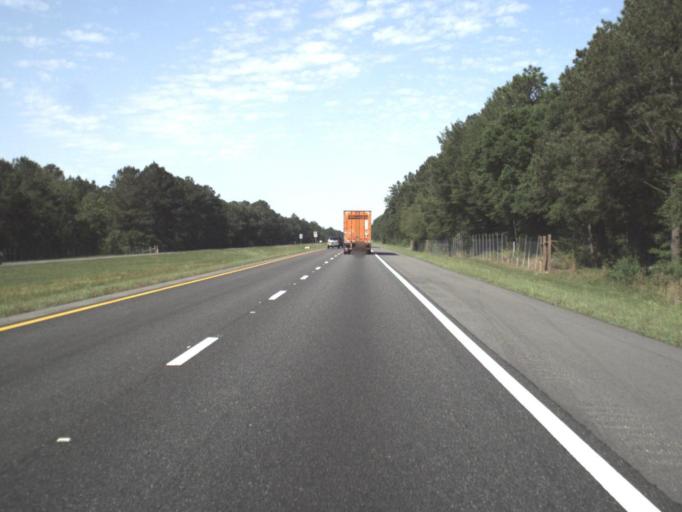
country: US
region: Florida
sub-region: Holmes County
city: Bonifay
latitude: 30.7495
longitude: -85.8627
